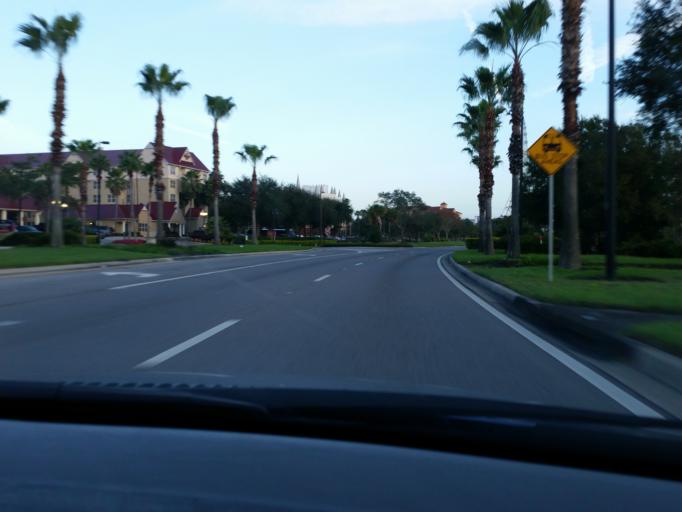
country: US
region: Florida
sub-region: Orange County
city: Doctor Phillips
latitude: 28.4367
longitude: -81.4677
